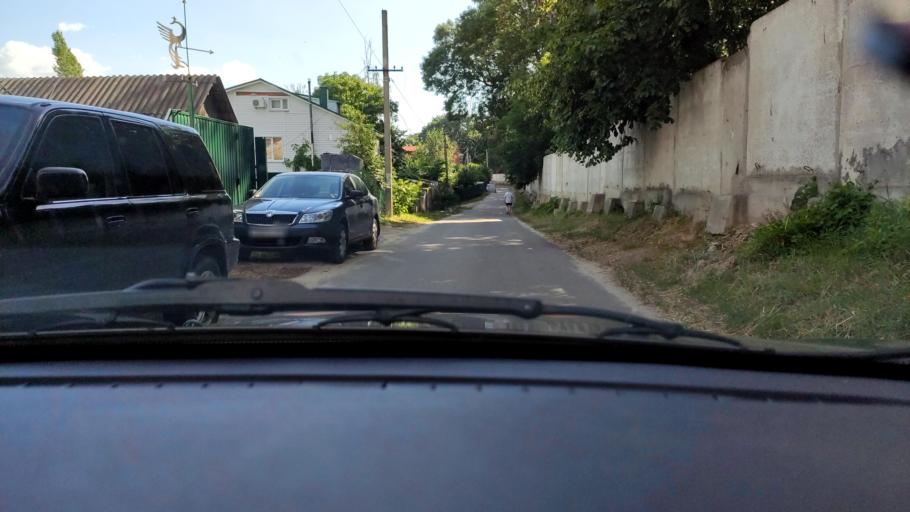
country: RU
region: Voronezj
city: Ramon'
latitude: 51.8236
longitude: 39.2696
